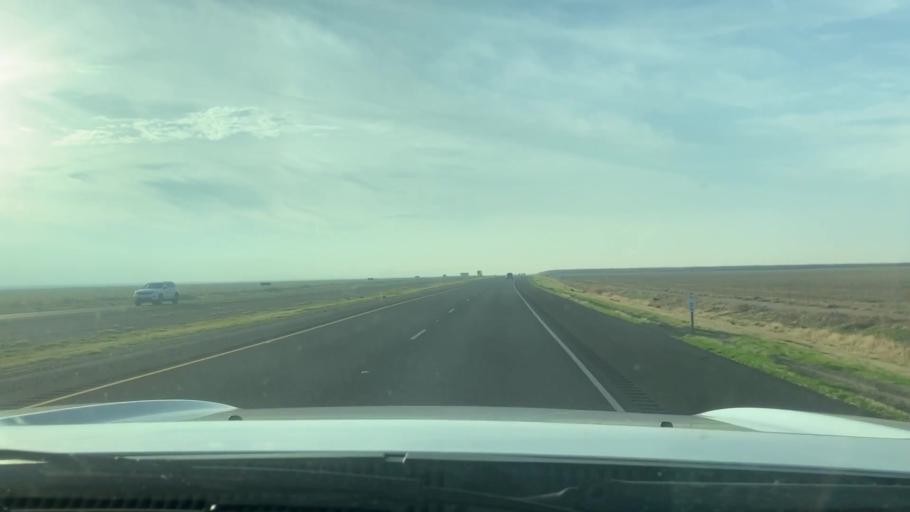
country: US
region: California
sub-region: Kern County
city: Lost Hills
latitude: 35.6149
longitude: -119.8771
